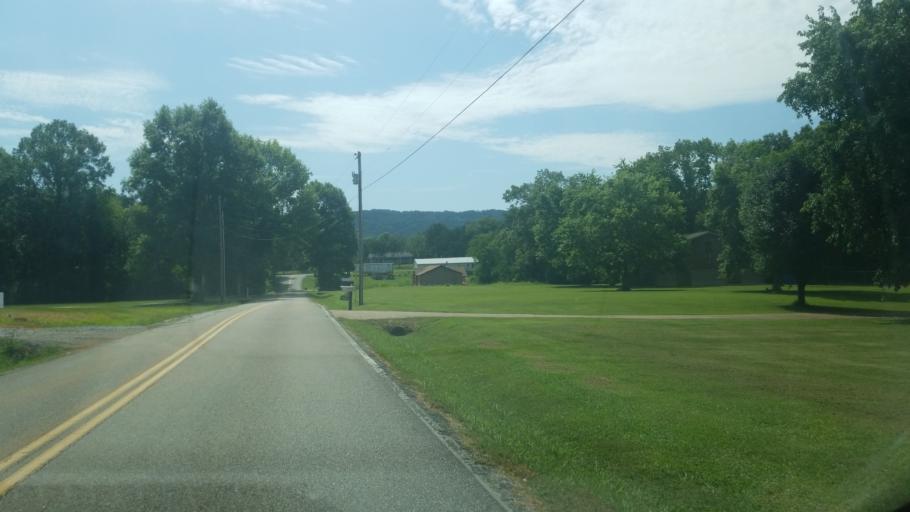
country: US
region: Tennessee
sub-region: Hamilton County
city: Lakesite
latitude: 35.2128
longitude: -85.0227
